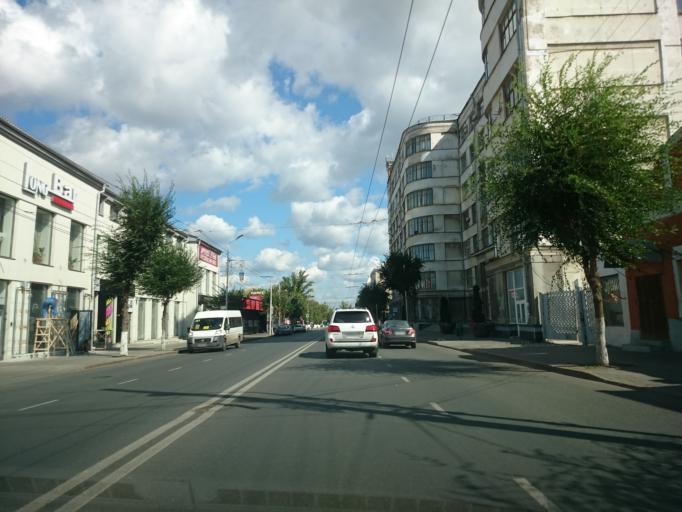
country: RU
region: Samara
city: Rozhdestveno
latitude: 53.1938
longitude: 50.0931
